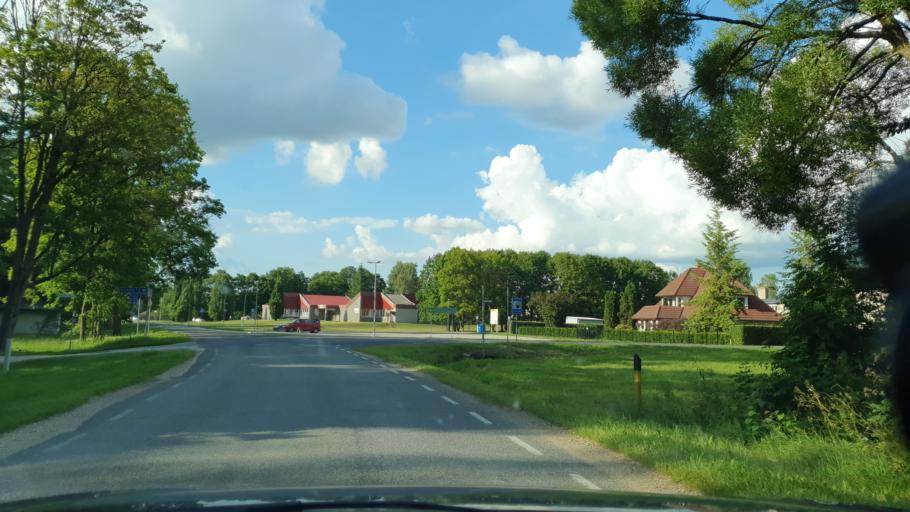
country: EE
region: Jogevamaa
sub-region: Tabivere vald
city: Tabivere
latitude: 58.6834
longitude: 26.5858
